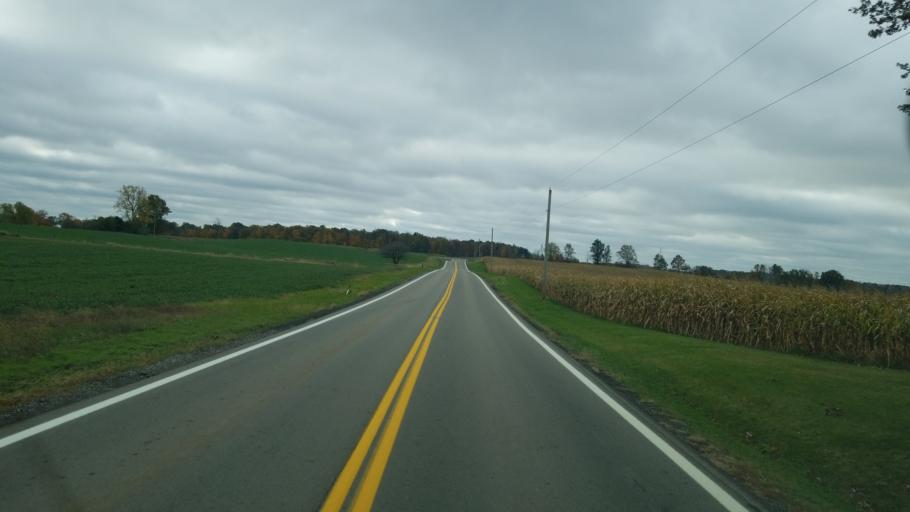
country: US
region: Ohio
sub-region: Richland County
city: Shelby
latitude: 40.9121
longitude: -82.7360
